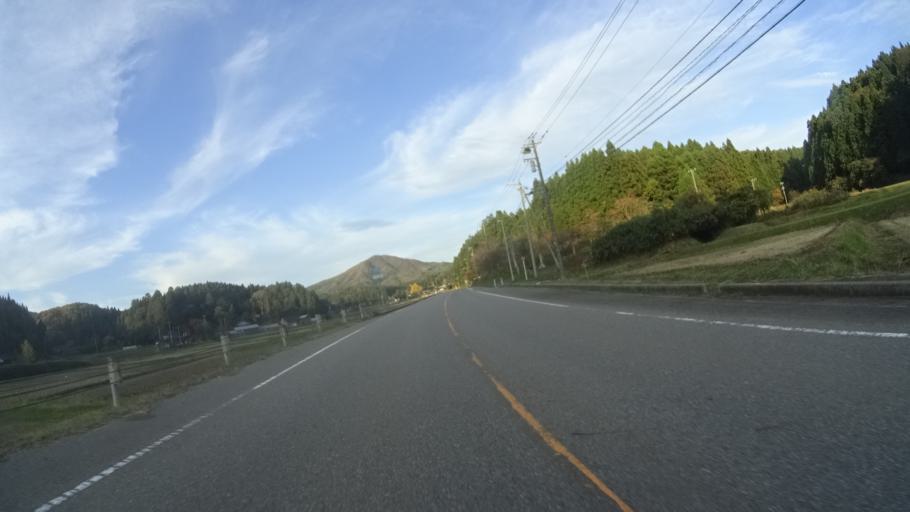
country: JP
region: Ishikawa
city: Nanao
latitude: 37.1854
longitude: 136.7143
